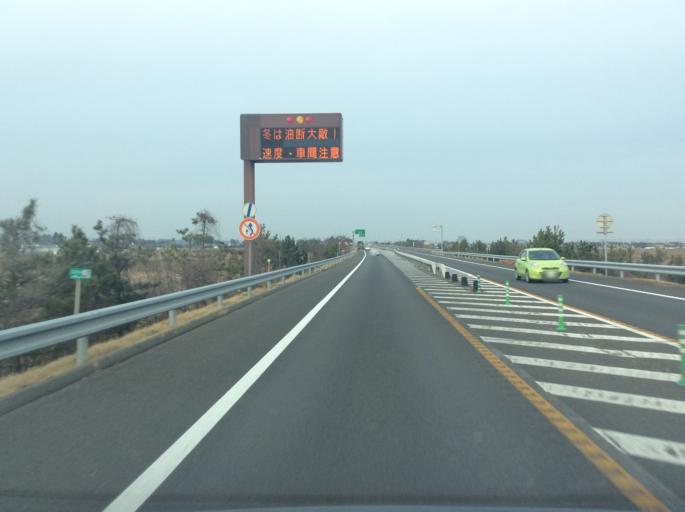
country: JP
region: Miyagi
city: Iwanuma
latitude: 38.1006
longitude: 140.8890
